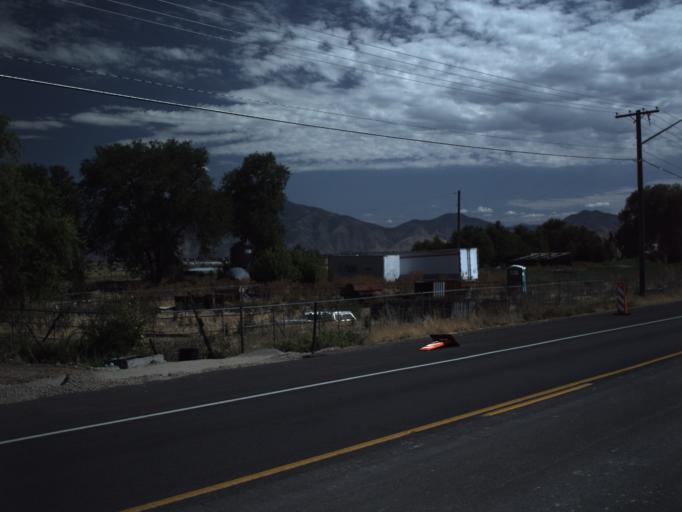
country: US
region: Utah
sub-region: Utah County
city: Payson
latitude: 40.0456
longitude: -111.7095
